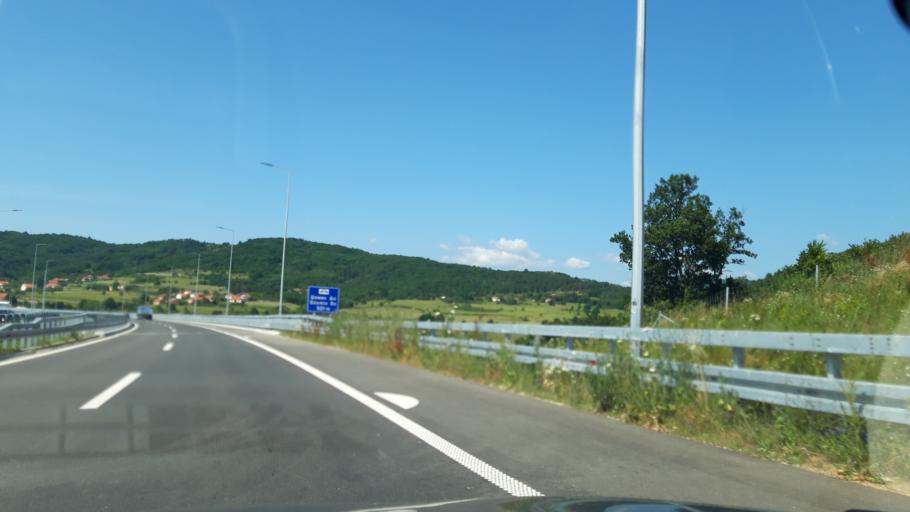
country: RS
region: Central Serbia
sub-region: Pcinjski Okrug
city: Vladicin Han
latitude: 42.7192
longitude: 22.0763
